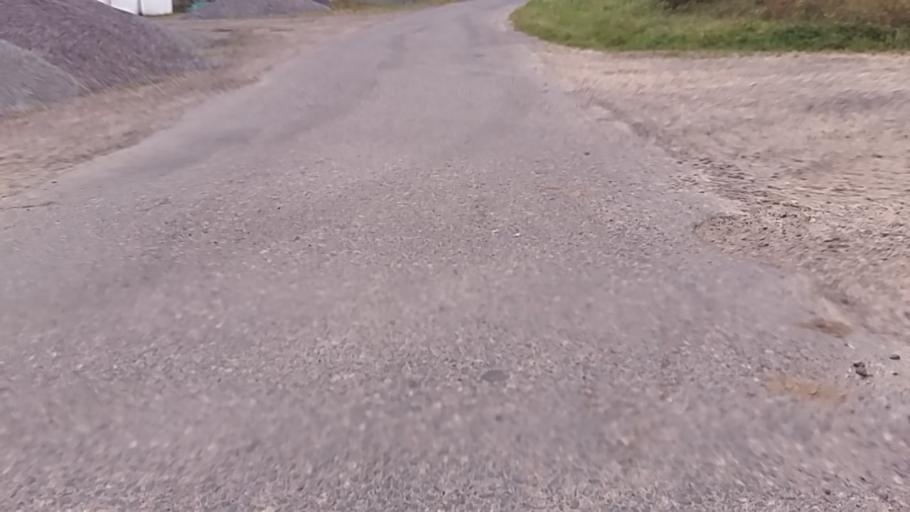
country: SE
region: Joenkoeping
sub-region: Jonkopings Kommun
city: Taberg
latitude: 57.7074
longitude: 14.1103
